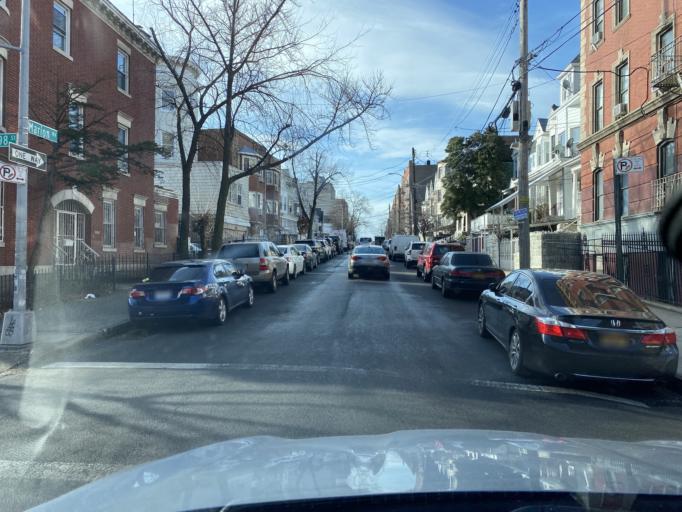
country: US
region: New York
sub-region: Bronx
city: The Bronx
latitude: 40.8673
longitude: -73.8869
